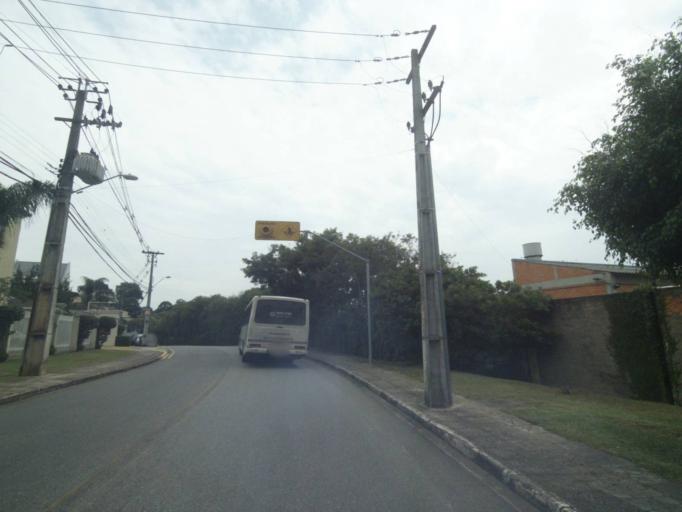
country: BR
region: Parana
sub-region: Curitiba
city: Curitiba
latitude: -25.4085
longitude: -49.3040
